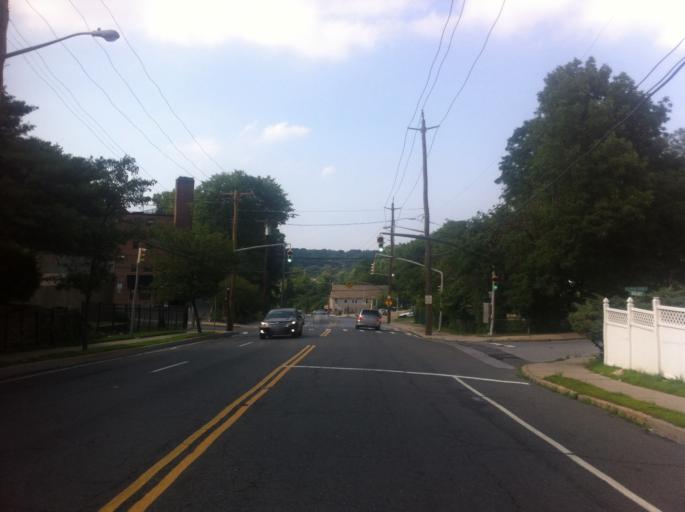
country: US
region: New York
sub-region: Nassau County
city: Glen Cove
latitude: 40.8545
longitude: -73.6343
